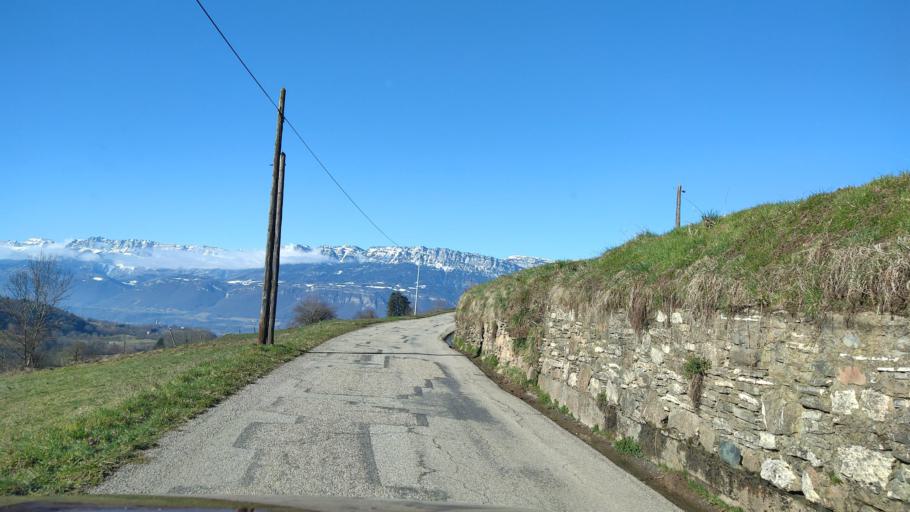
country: FR
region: Rhone-Alpes
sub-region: Departement de la Savoie
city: La Rochette
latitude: 45.4484
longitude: 6.0812
